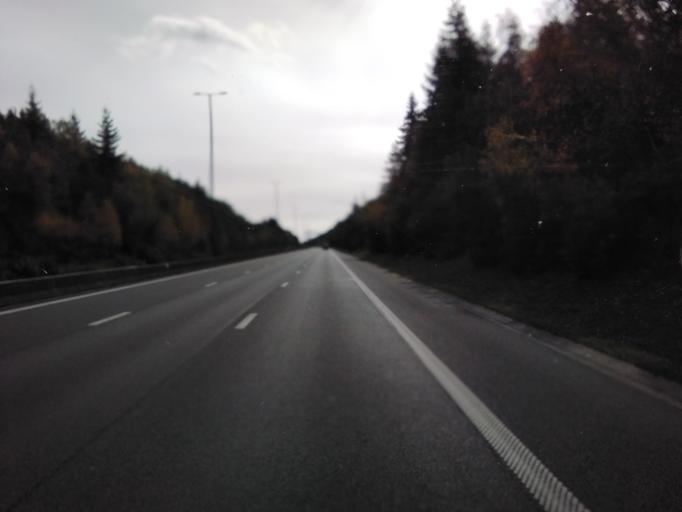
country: BE
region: Wallonia
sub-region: Province du Luxembourg
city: Tellin
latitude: 50.0742
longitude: 5.1794
